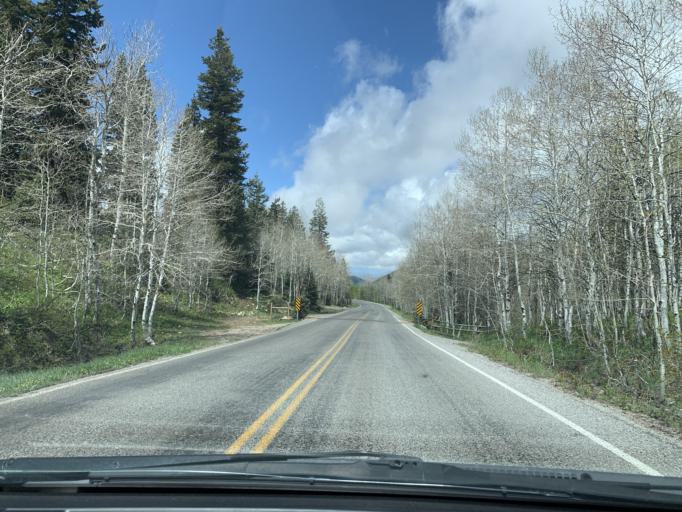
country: US
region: Utah
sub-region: Utah County
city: Woodland Hills
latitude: 39.9398
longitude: -111.6405
